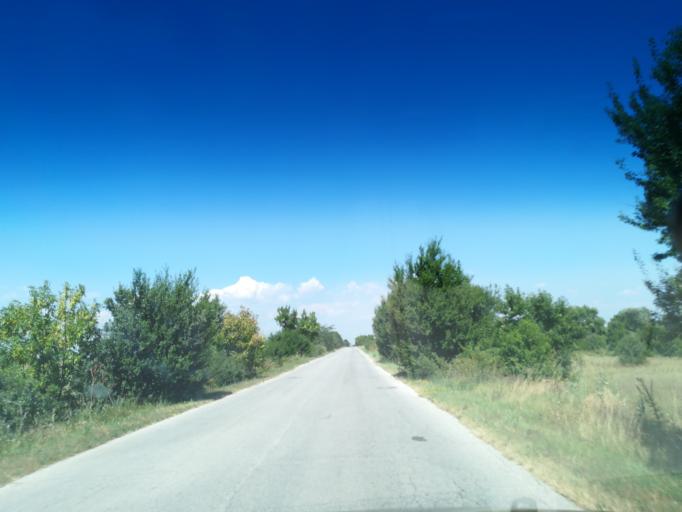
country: BG
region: Plovdiv
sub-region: Obshtina Sadovo
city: Sadovo
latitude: 42.0494
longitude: 25.1446
